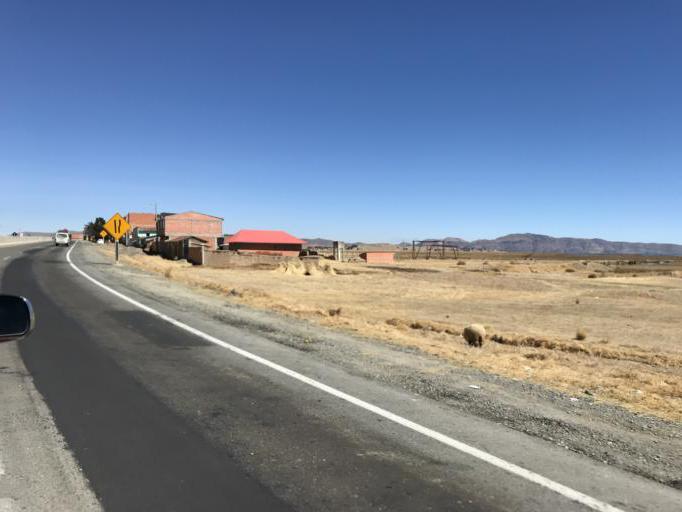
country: BO
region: La Paz
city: Batallas
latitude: -16.2480
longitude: -68.5694
